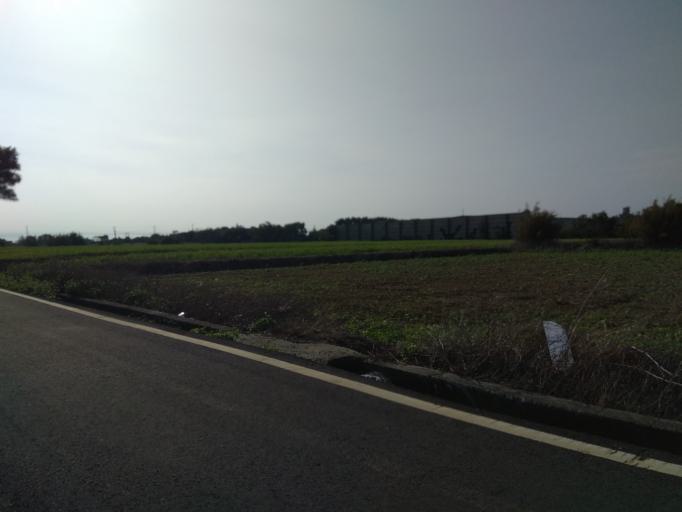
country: TW
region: Taiwan
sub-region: Hsinchu
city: Zhubei
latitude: 25.0047
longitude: 121.0454
